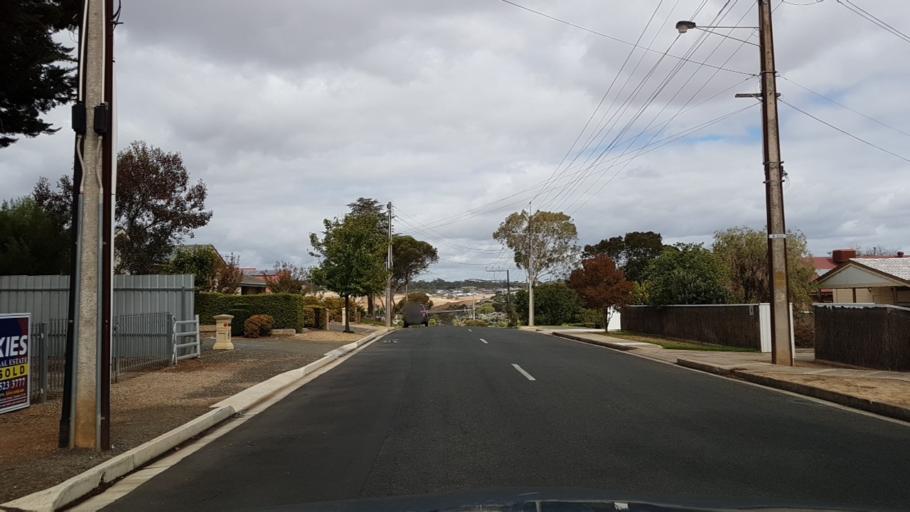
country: AU
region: South Australia
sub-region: Gawler
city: Gawler
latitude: -34.6053
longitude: 138.7542
